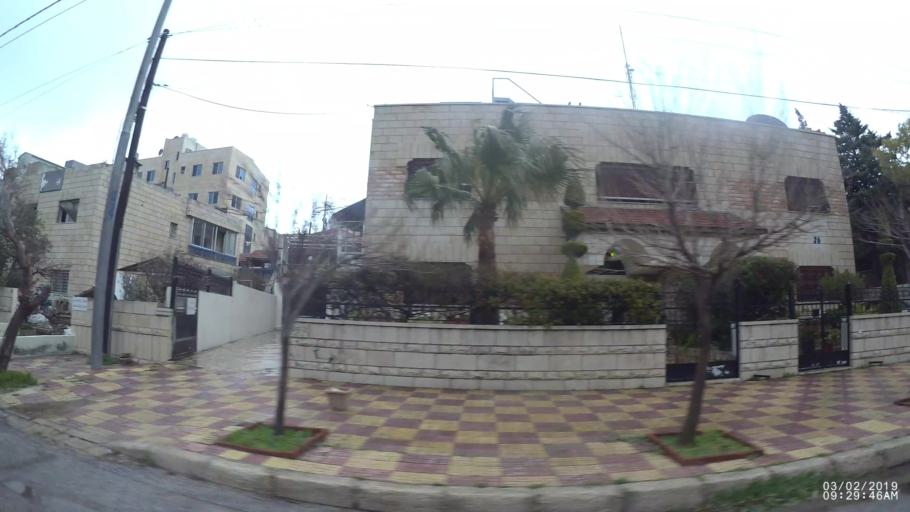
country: JO
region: Amman
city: Amman
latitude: 31.9494
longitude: 35.9044
